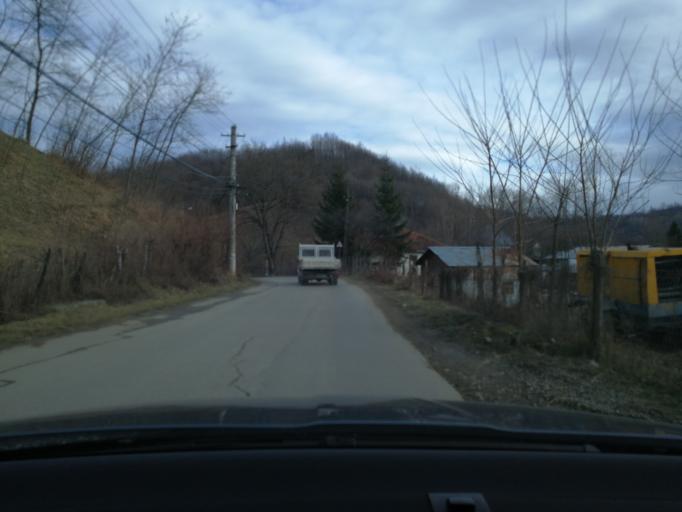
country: RO
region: Prahova
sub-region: Oras Breaza
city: Valea Tarsei
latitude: 45.1815
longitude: 25.6404
